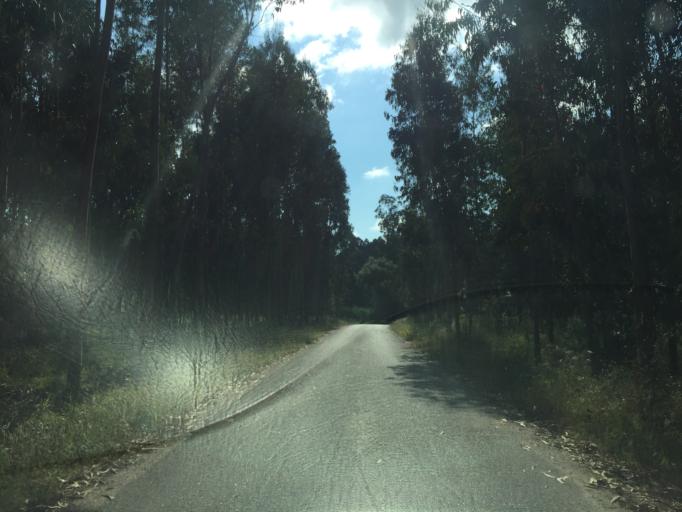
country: PT
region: Leiria
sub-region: Pombal
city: Lourical
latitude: 39.9664
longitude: -8.7989
